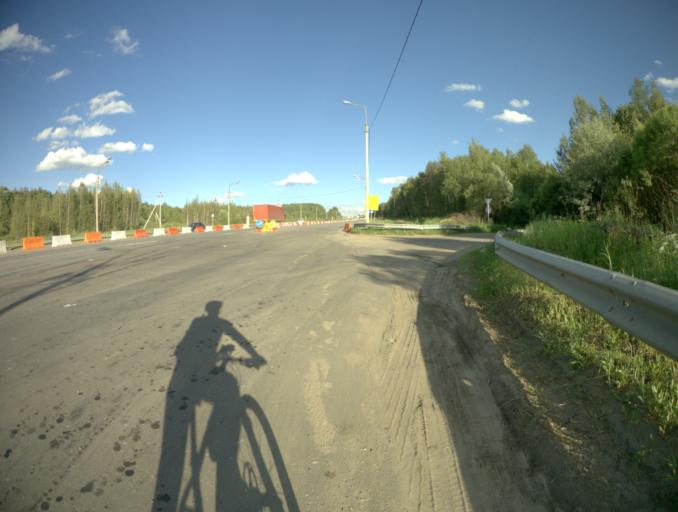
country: RU
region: Vladimir
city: Kommunar
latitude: 56.0776
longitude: 40.4770
